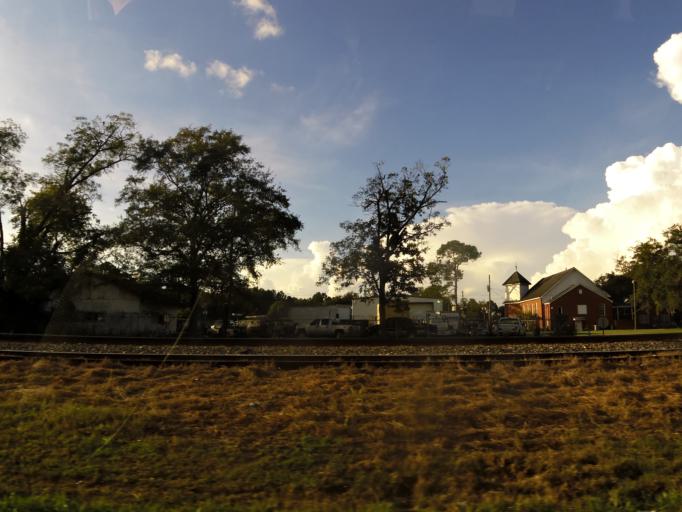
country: US
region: Georgia
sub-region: Lowndes County
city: Valdosta
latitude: 30.8230
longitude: -83.2958
